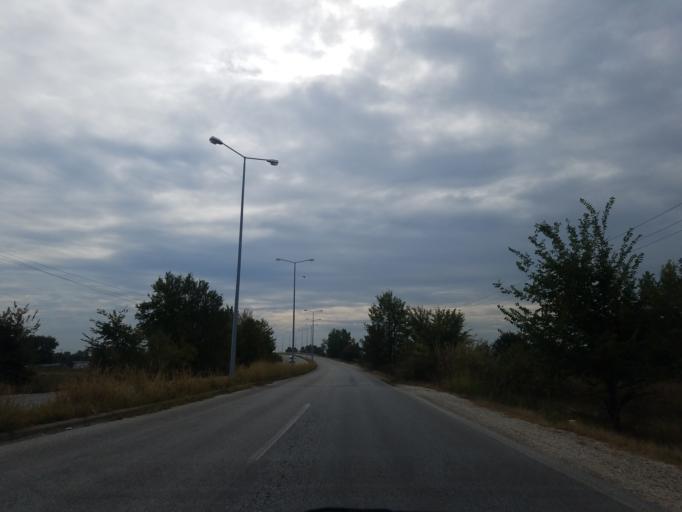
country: GR
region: Thessaly
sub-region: Trikala
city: Pyrgetos
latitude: 39.5229
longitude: 21.7522
